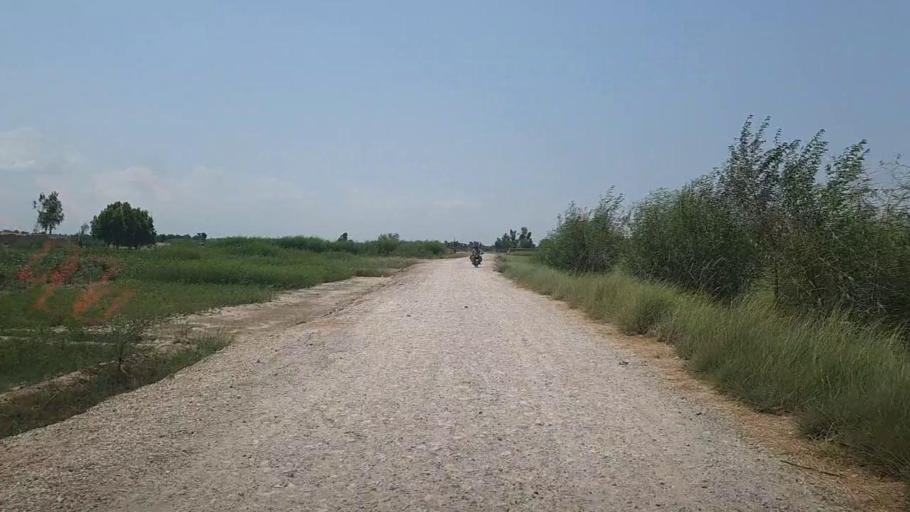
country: PK
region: Sindh
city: Ubauro
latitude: 28.1664
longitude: 69.7636
